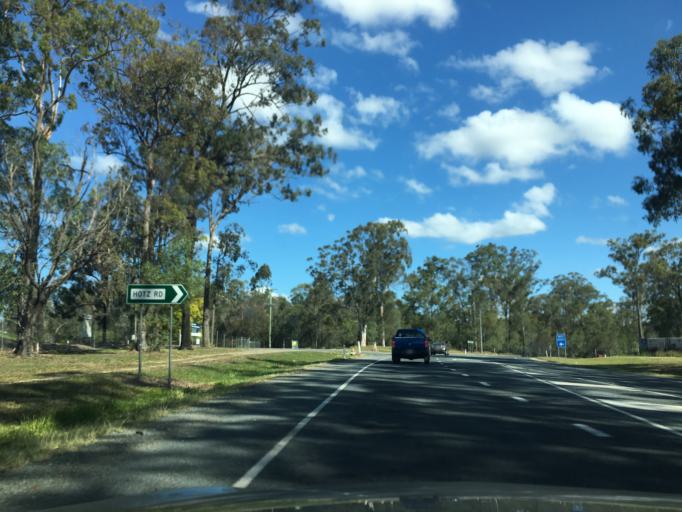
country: AU
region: Queensland
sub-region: Logan
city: Chambers Flat
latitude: -27.7866
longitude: 153.1003
